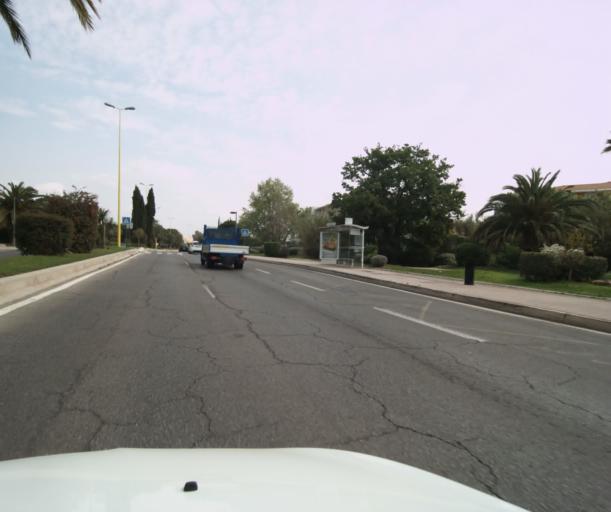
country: FR
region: Provence-Alpes-Cote d'Azur
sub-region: Departement du Var
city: La Garde
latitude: 43.1343
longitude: 6.0188
